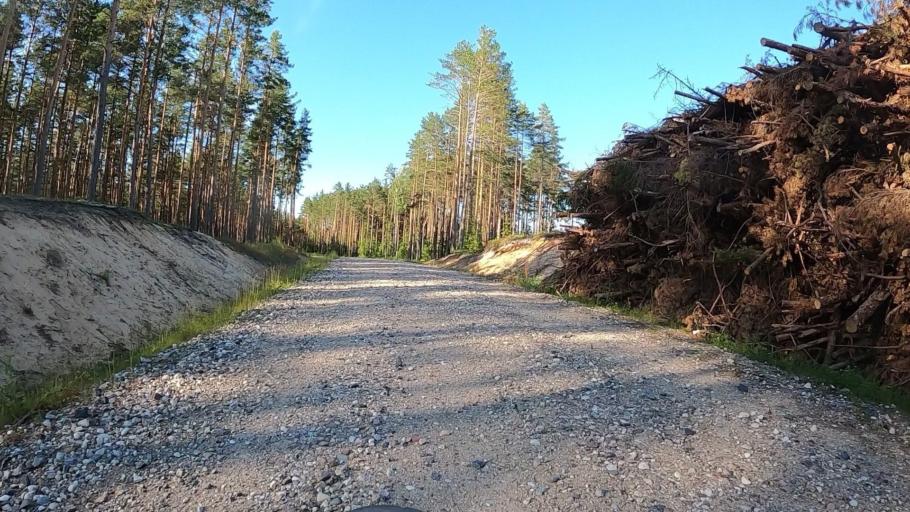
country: LV
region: Carnikava
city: Carnikava
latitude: 57.1083
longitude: 24.2521
